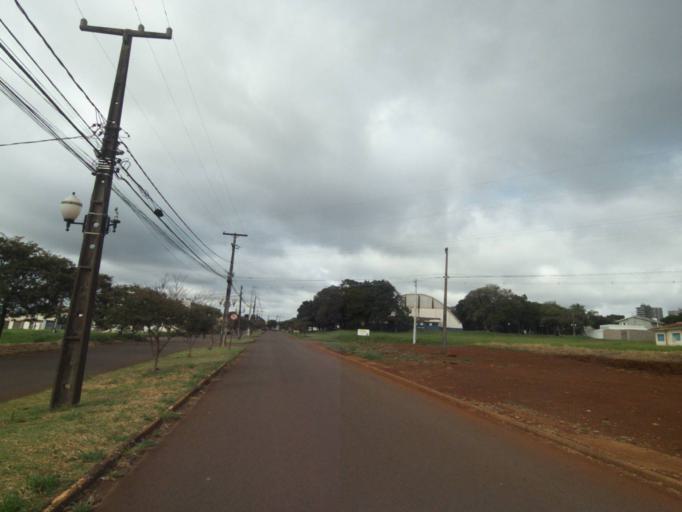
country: BR
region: Parana
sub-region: Campo Mourao
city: Campo Mourao
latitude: -24.0379
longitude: -52.3635
